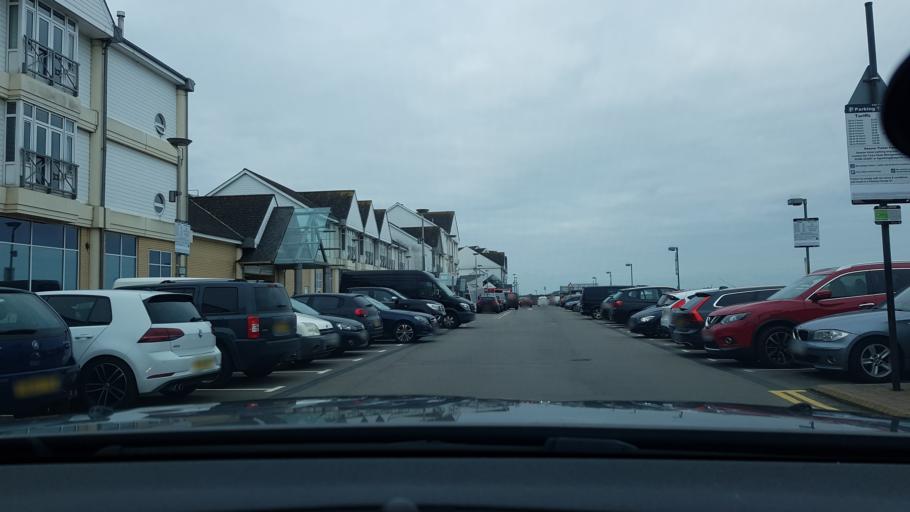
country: GB
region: England
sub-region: Southampton
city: Southampton
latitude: 50.8956
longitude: -1.4052
